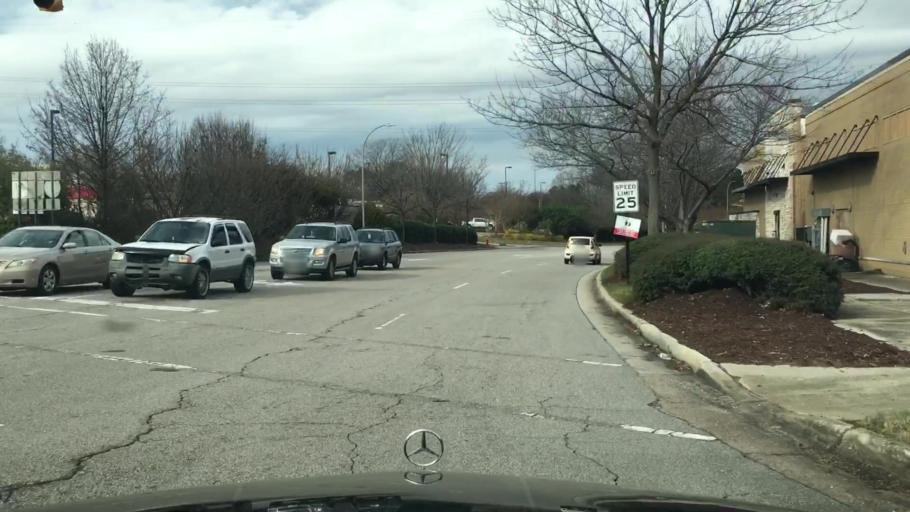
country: US
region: North Carolina
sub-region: Wake County
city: Cary
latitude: 35.7597
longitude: -78.7413
